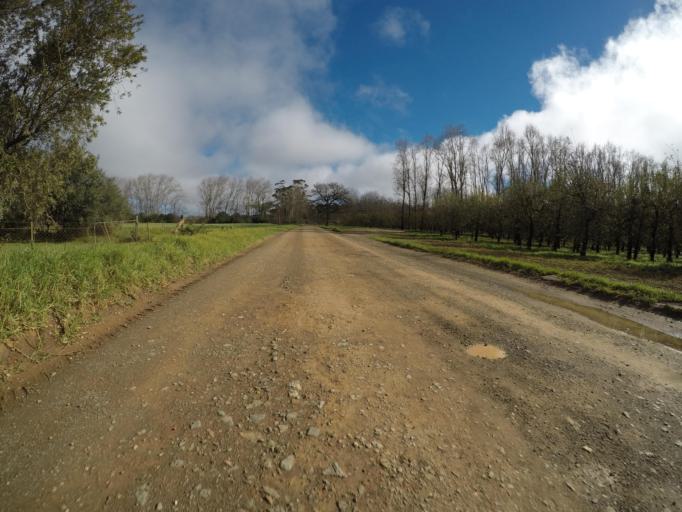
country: ZA
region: Western Cape
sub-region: Cape Winelands District Municipality
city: Ashton
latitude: -34.1257
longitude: 19.8130
